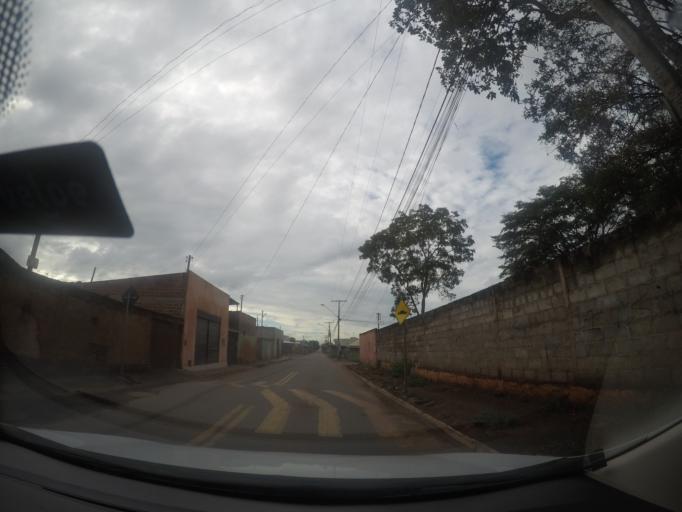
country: BR
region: Goias
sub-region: Goiania
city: Goiania
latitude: -16.6171
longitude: -49.3305
